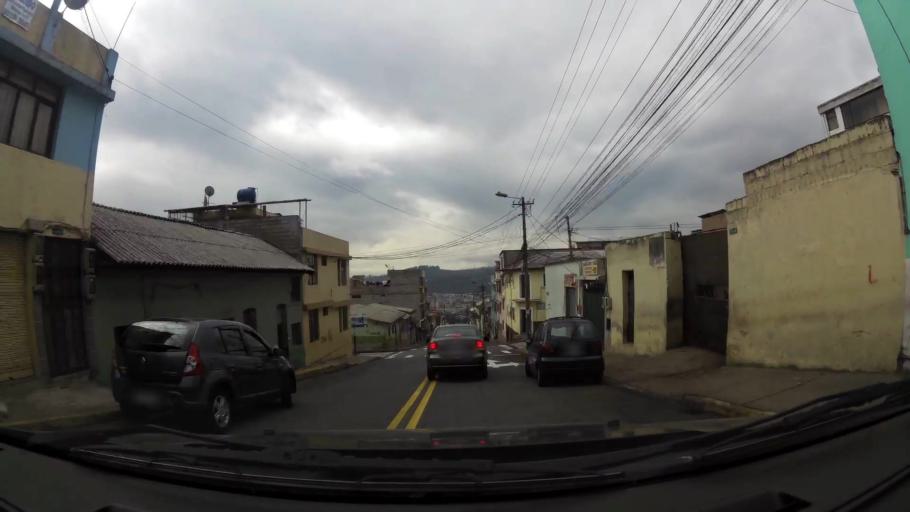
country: EC
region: Pichincha
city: Quito
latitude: -0.2110
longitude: -78.5129
